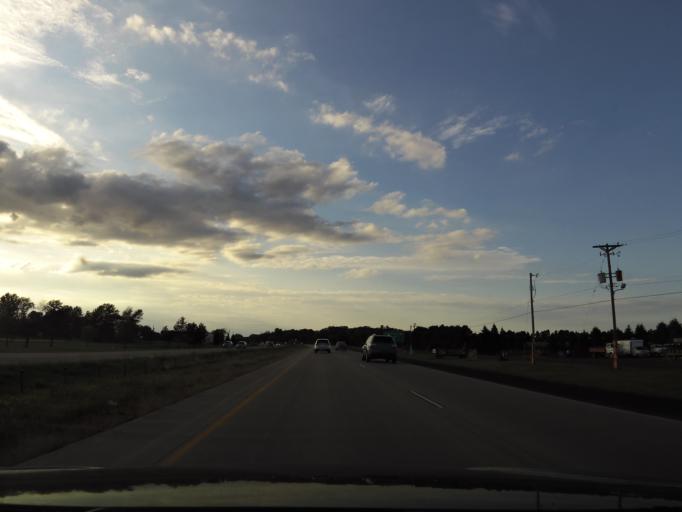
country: US
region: Minnesota
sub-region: Dakota County
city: Hastings
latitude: 44.7918
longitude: -92.8857
